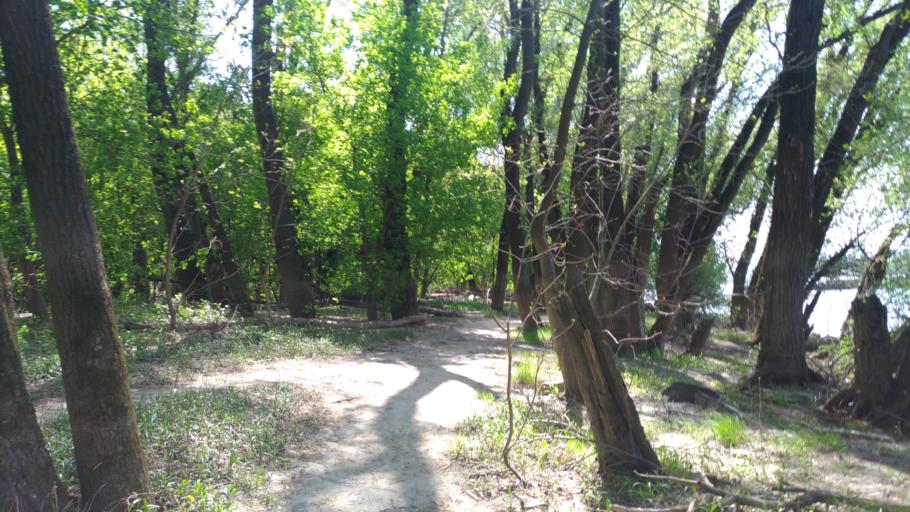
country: HU
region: Budapest
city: Budapest IV. keruelet
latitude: 47.5820
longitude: 19.0740
